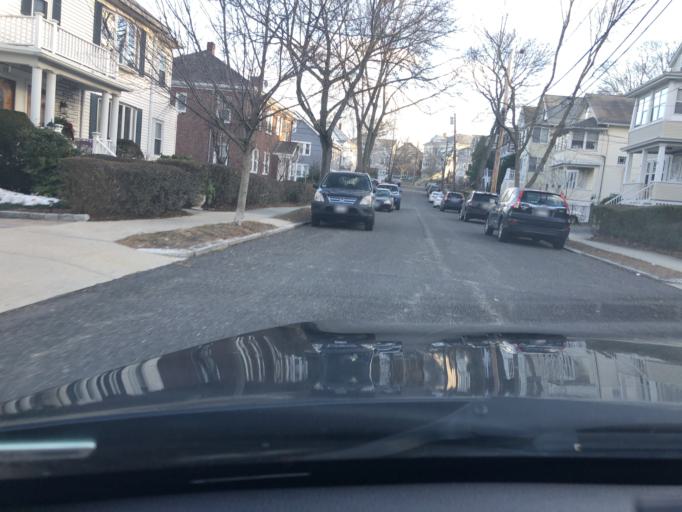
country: US
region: Massachusetts
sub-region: Middlesex County
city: Arlington
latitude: 42.4178
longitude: -71.1683
